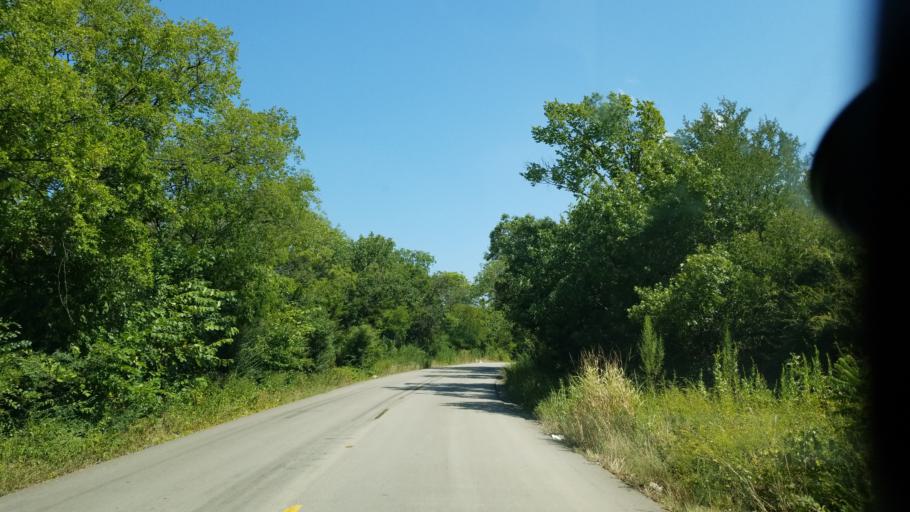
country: US
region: Texas
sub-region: Dallas County
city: Cockrell Hill
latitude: 32.7065
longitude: -96.9256
